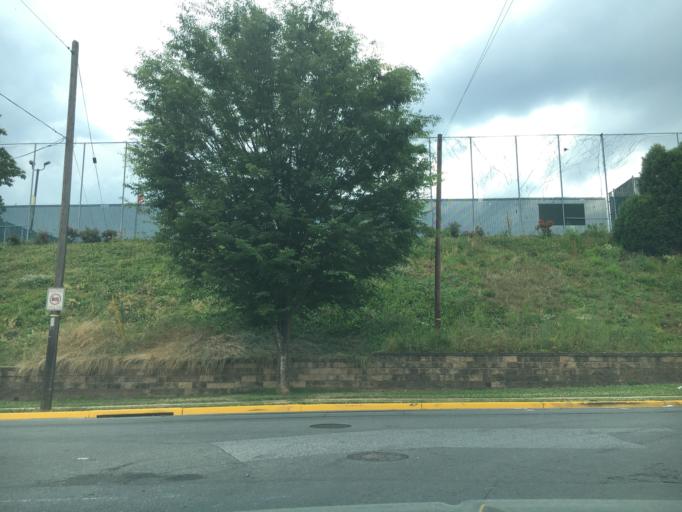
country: US
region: Pennsylvania
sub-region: Berks County
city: Reading
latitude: 40.3401
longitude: -75.9315
